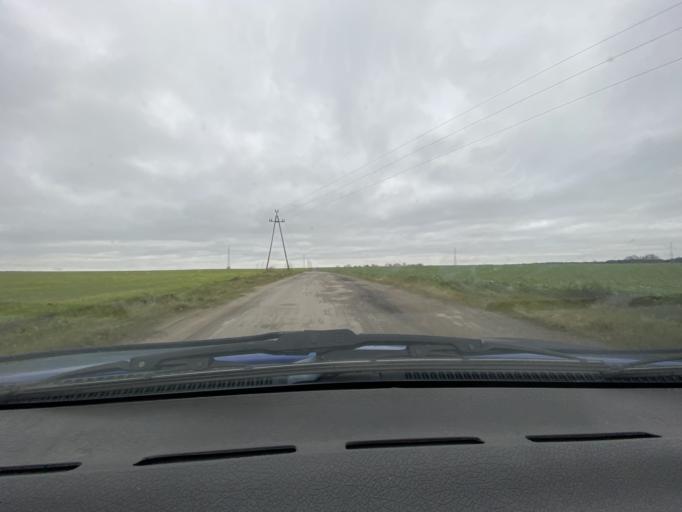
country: PL
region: West Pomeranian Voivodeship
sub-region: Powiat gryficki
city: Gryfice
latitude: 53.9557
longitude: 15.2554
